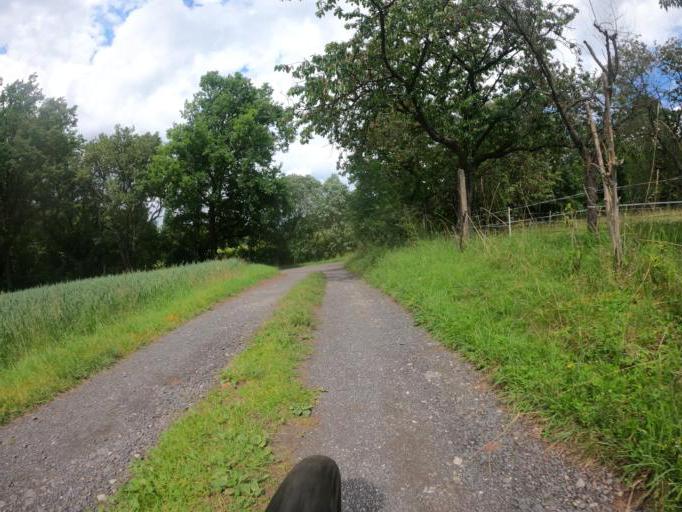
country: DE
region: Hesse
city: Witzenhausen
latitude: 51.2754
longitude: 9.8489
